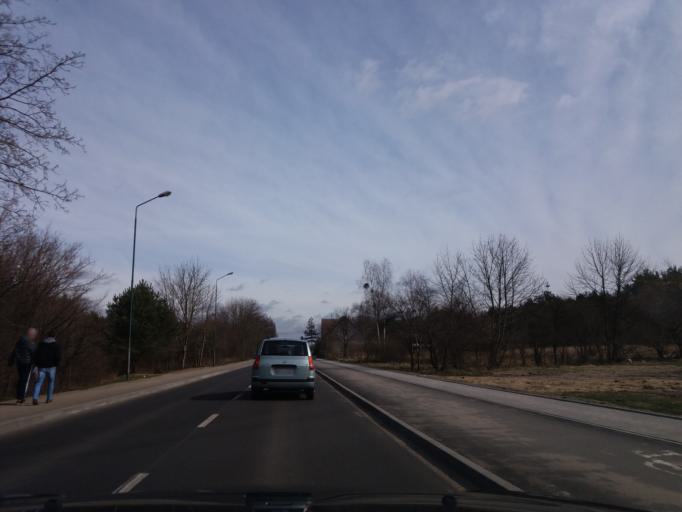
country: PL
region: West Pomeranian Voivodeship
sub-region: Powiat drawski
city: Kalisz Pomorski
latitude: 53.2864
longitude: 15.8908
